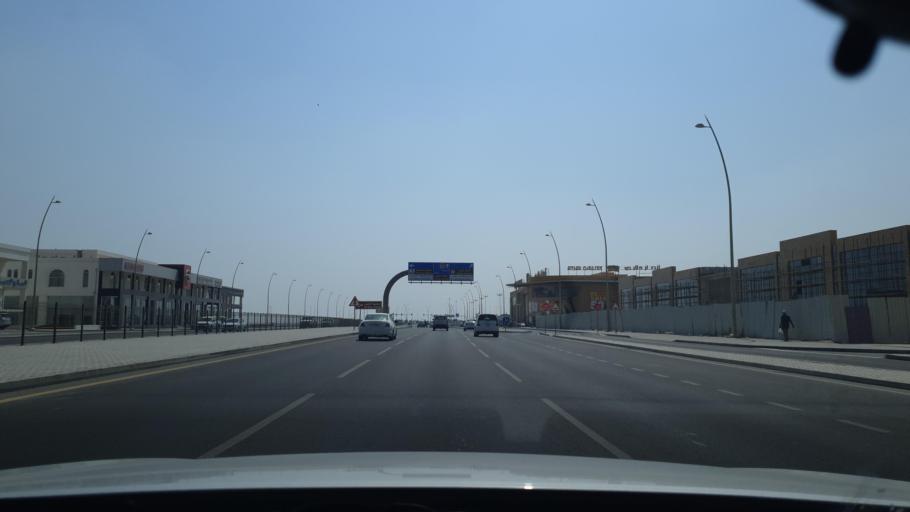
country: QA
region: Al Khawr
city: Al Khawr
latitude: 25.6684
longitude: 51.5008
